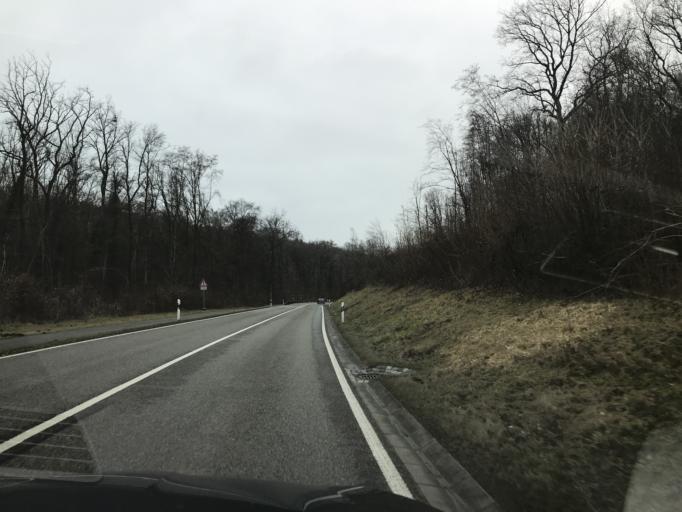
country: DE
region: Baden-Wuerttemberg
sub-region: Regierungsbezirk Stuttgart
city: Wolfschlugen
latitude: 48.6353
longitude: 9.3003
